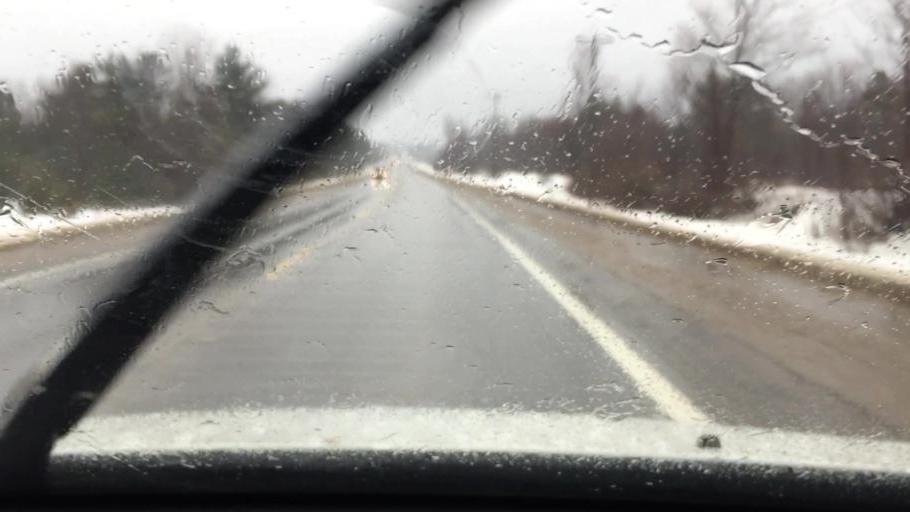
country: US
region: Michigan
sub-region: Charlevoix County
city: Charlevoix
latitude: 45.2742
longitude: -85.2188
